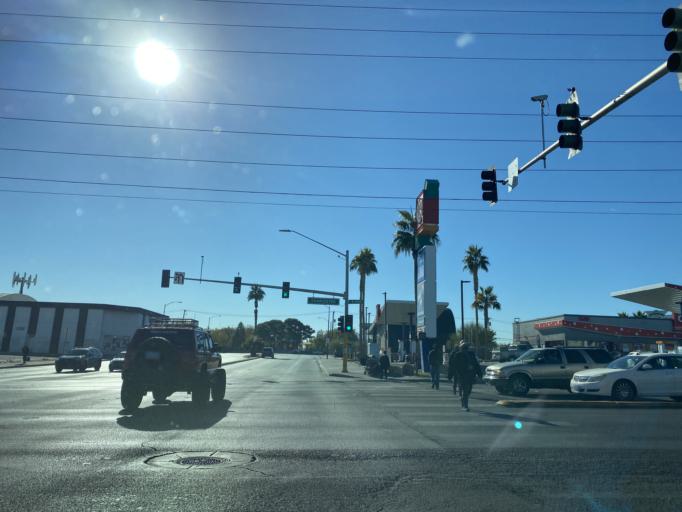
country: US
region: Nevada
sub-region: Clark County
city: Las Vegas
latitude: 36.1591
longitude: -115.1369
